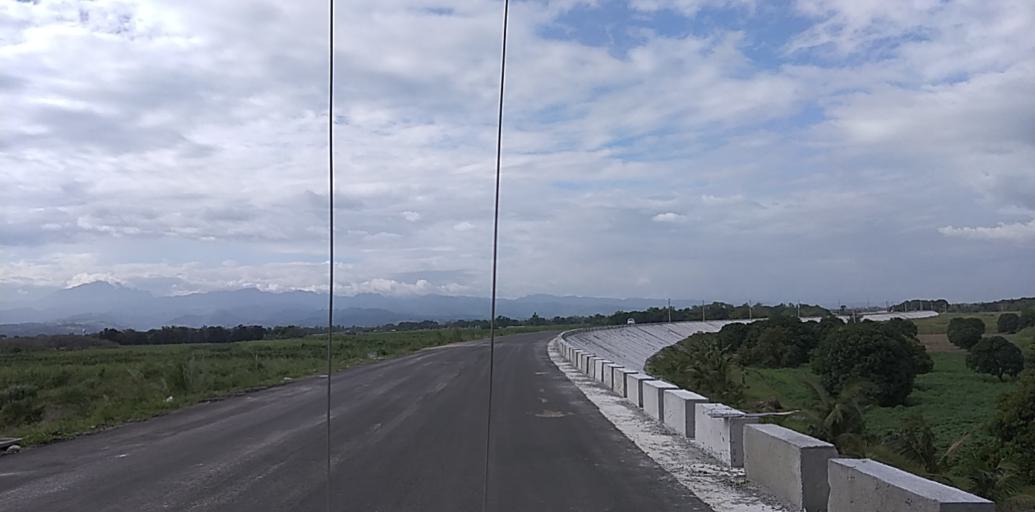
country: PH
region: Central Luzon
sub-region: Province of Pampanga
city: Pulung Santol
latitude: 15.0617
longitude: 120.5627
